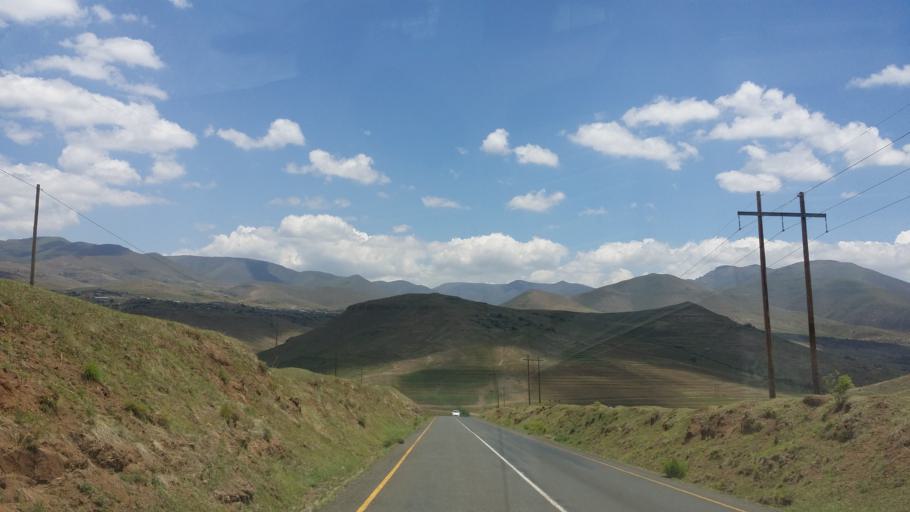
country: LS
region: Mokhotlong
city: Mokhotlong
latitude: -29.2139
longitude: 28.8931
